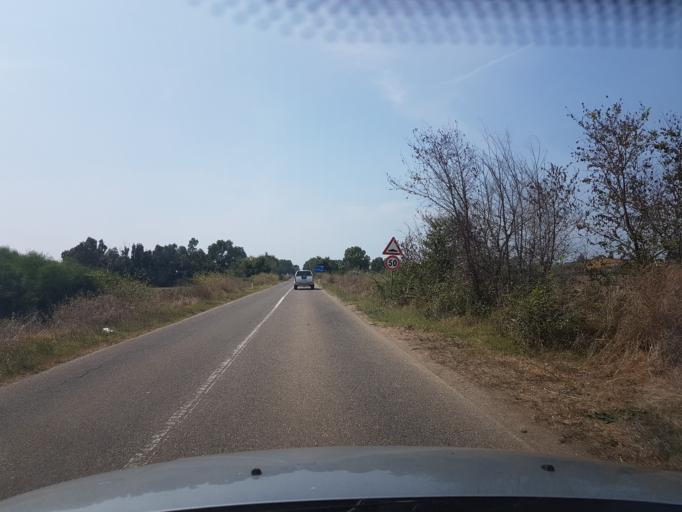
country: IT
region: Sardinia
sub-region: Provincia di Oristano
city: Solanas
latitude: 39.9192
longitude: 8.5506
